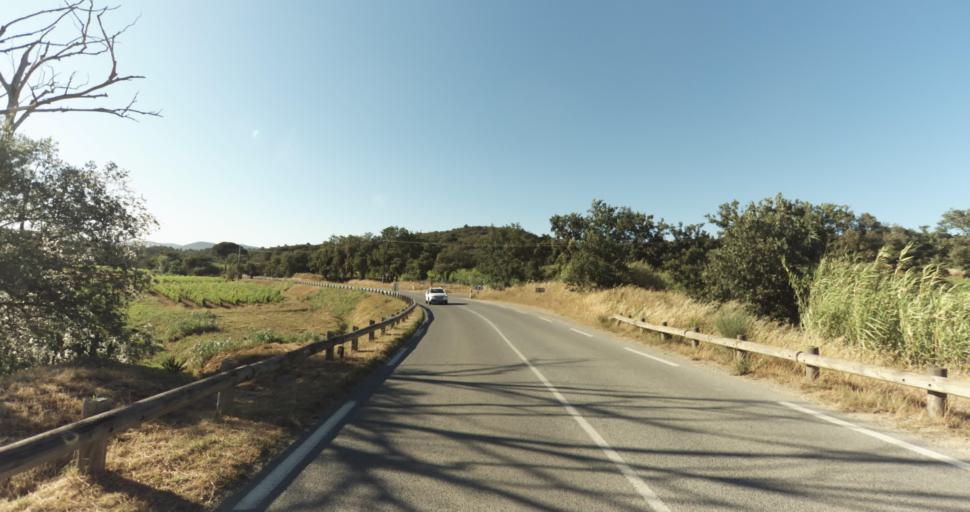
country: FR
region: Provence-Alpes-Cote d'Azur
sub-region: Departement du Var
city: Ramatuelle
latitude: 43.2351
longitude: 6.6106
